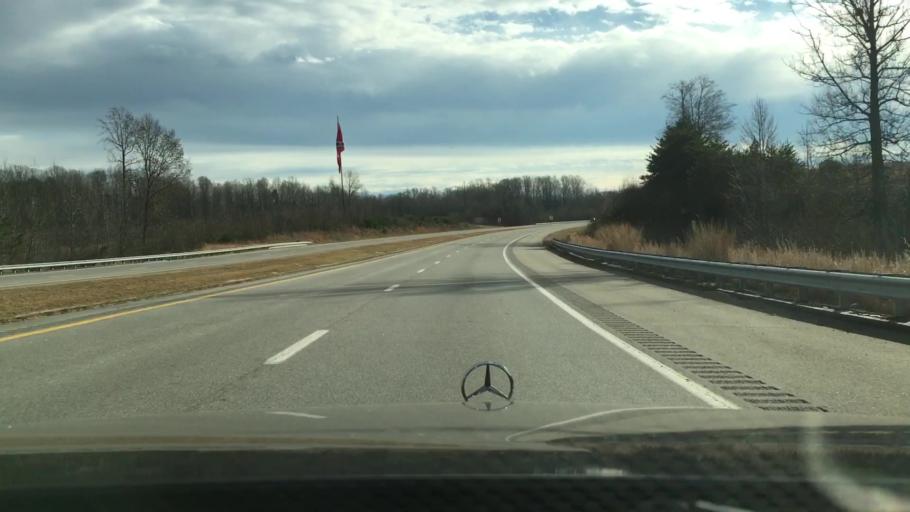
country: US
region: Virginia
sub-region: Pittsylvania County
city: Mount Hermon
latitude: 36.6922
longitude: -79.3611
